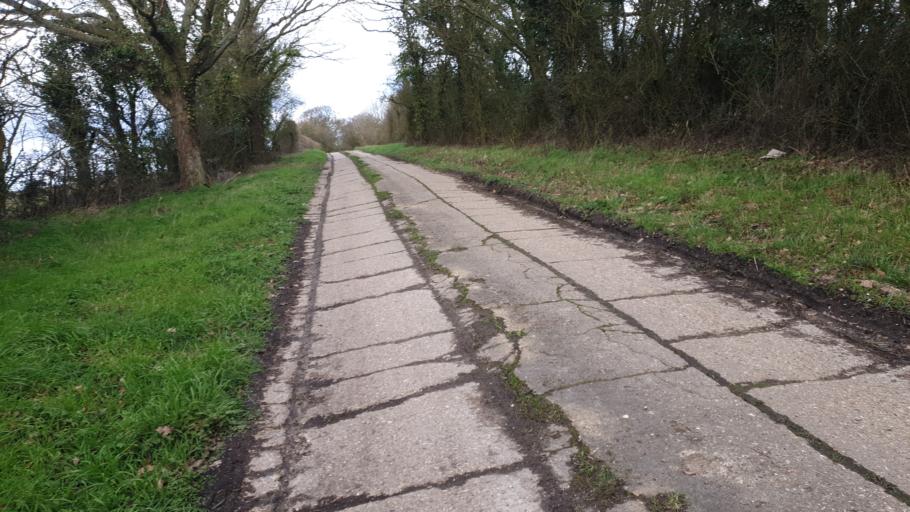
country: GB
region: England
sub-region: Essex
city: Little Clacton
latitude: 51.8301
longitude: 1.1721
